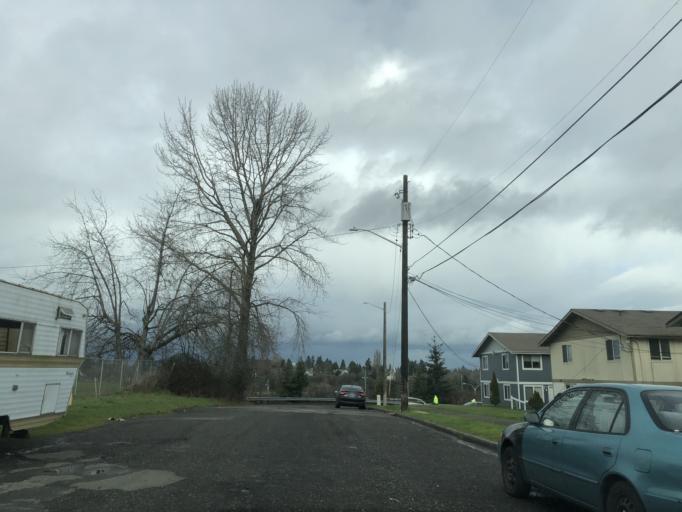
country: US
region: Washington
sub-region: Pierce County
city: Tacoma
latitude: 47.2293
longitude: -122.4571
